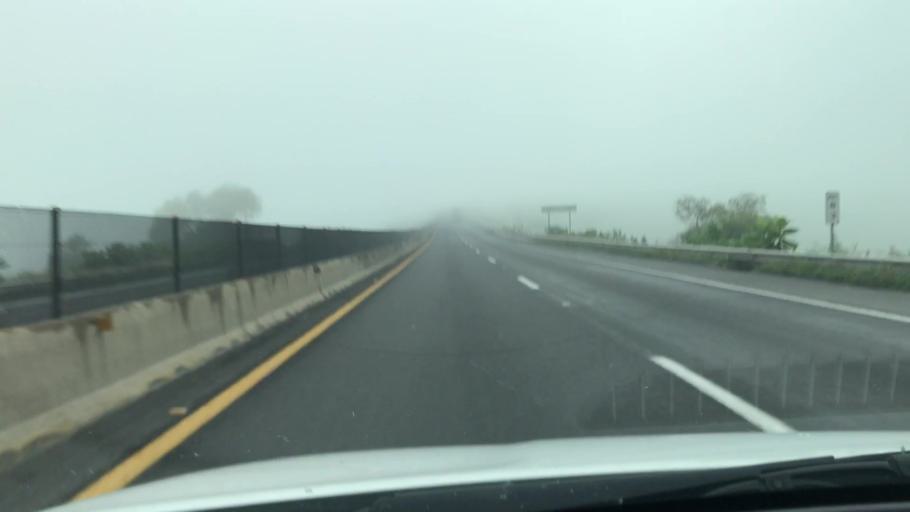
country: MX
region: Jalisco
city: Jalostotitlan
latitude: 21.0771
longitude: -102.5000
